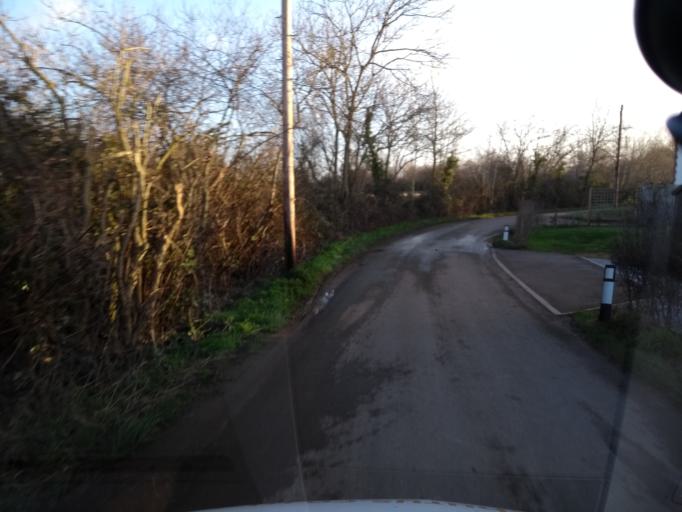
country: GB
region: England
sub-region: Somerset
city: Bridgwater
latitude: 51.1488
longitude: -3.0072
